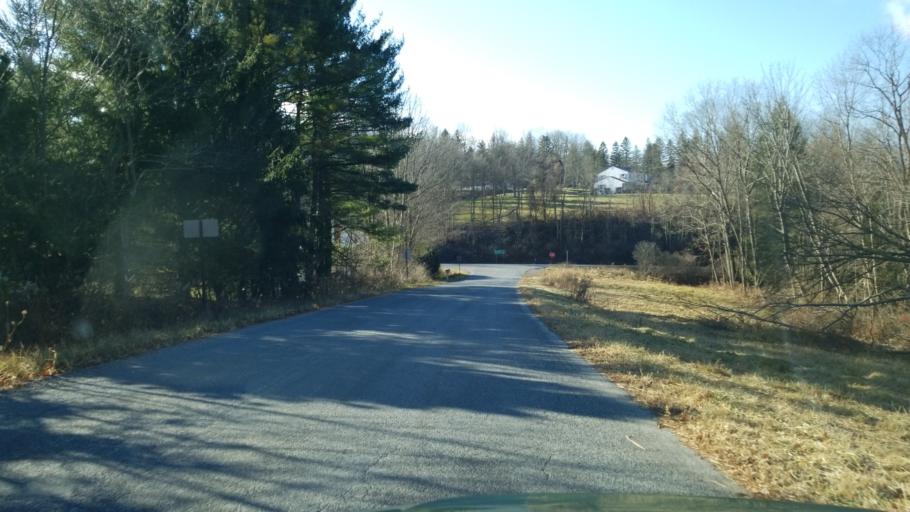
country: US
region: Pennsylvania
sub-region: Clearfield County
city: Clearfield
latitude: 41.0038
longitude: -78.4215
